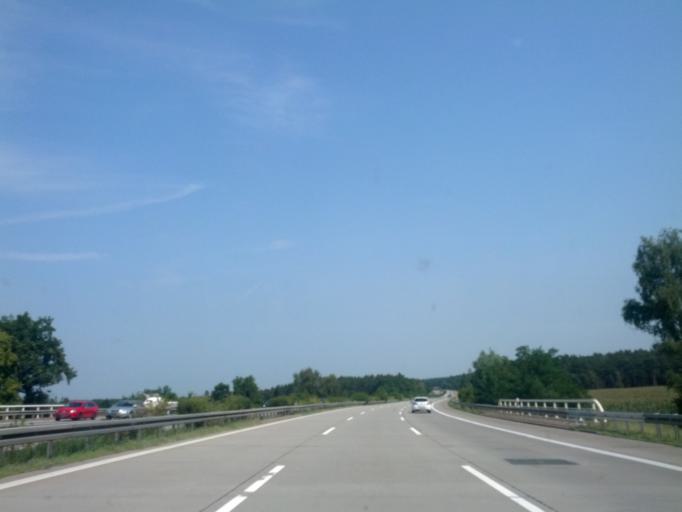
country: DE
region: Brandenburg
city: Niemegk
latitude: 52.0416
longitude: 12.6263
